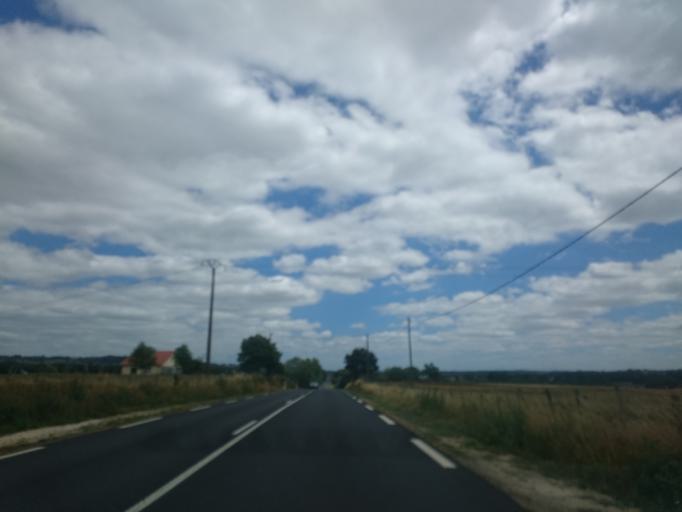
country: FR
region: Auvergne
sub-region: Departement du Cantal
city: Saint-Paul-des-Landes
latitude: 44.9506
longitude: 2.2936
